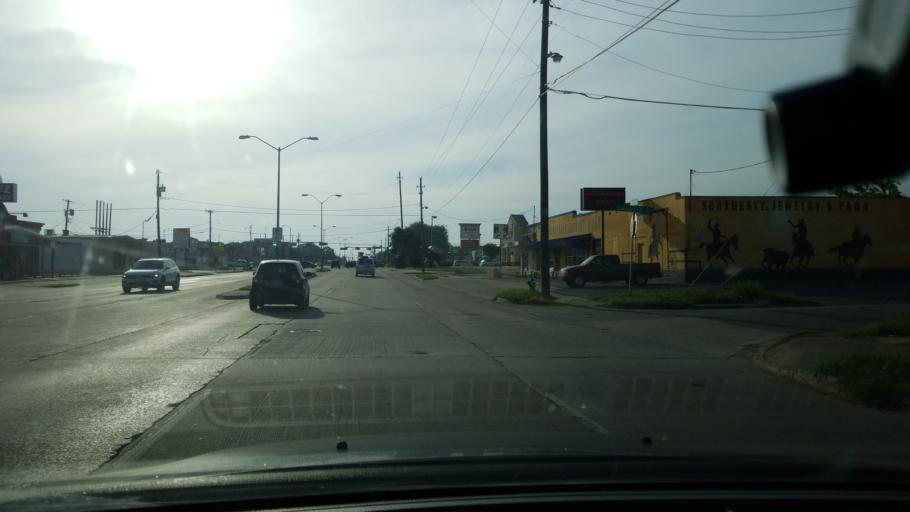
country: US
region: Texas
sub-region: Dallas County
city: Balch Springs
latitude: 32.7342
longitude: -96.6849
